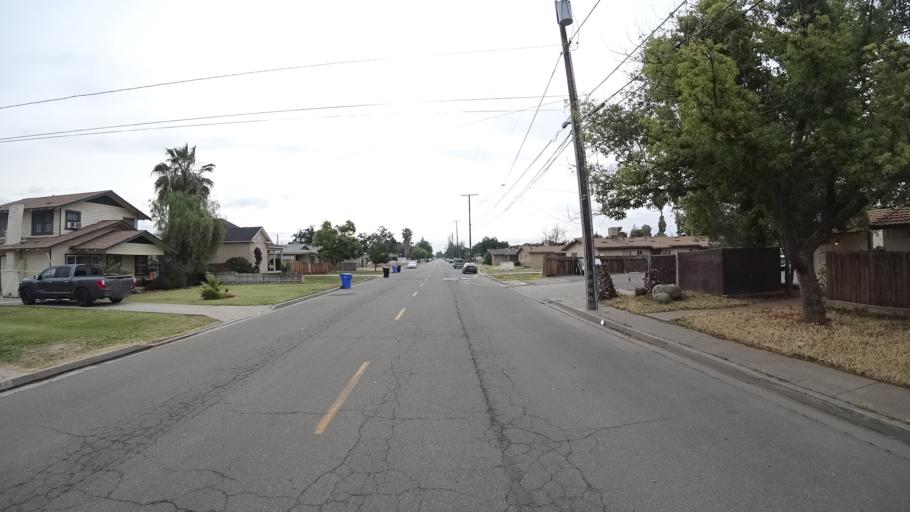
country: US
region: California
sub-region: Kings County
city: Hanford
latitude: 36.3371
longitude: -119.6423
